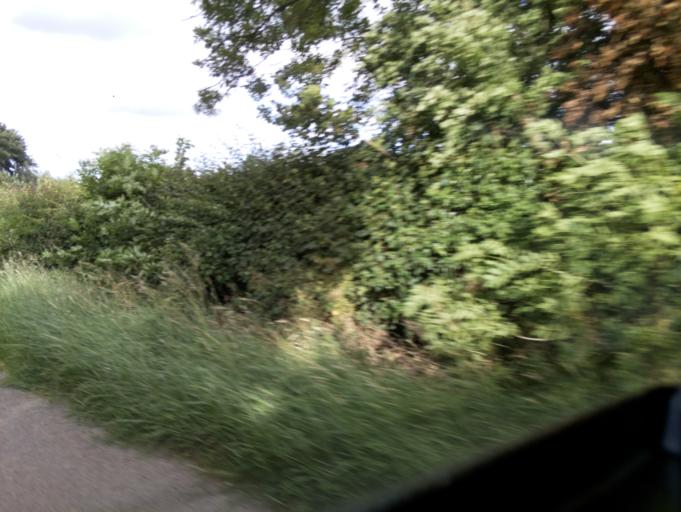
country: GB
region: England
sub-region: Gloucestershire
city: Chipping Campden
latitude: 52.0335
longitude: -1.7326
